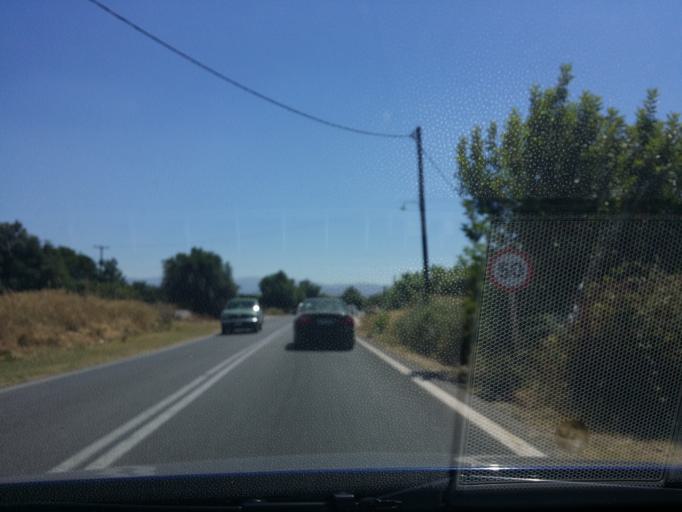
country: GR
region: Peloponnese
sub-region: Nomos Lakonias
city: Skala
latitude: 36.8445
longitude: 22.6442
